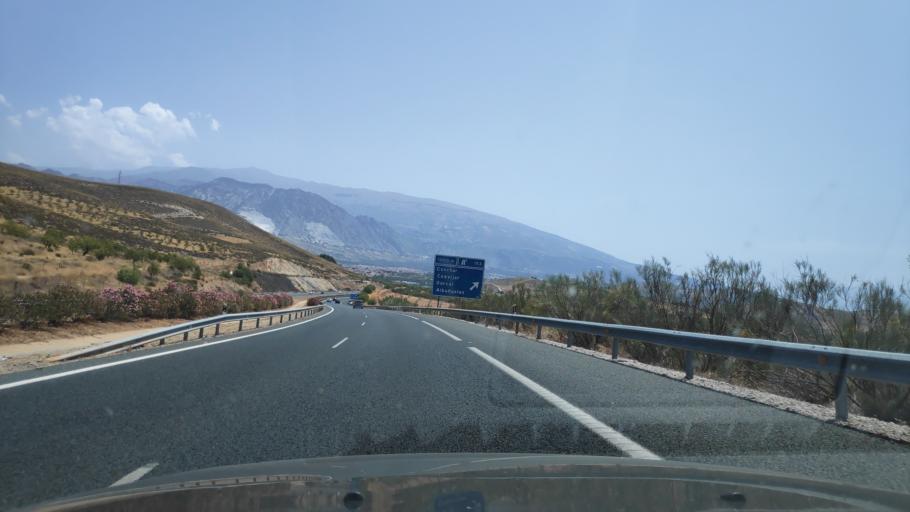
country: ES
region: Andalusia
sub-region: Provincia de Granada
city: Padul
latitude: 36.9911
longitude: -3.6221
